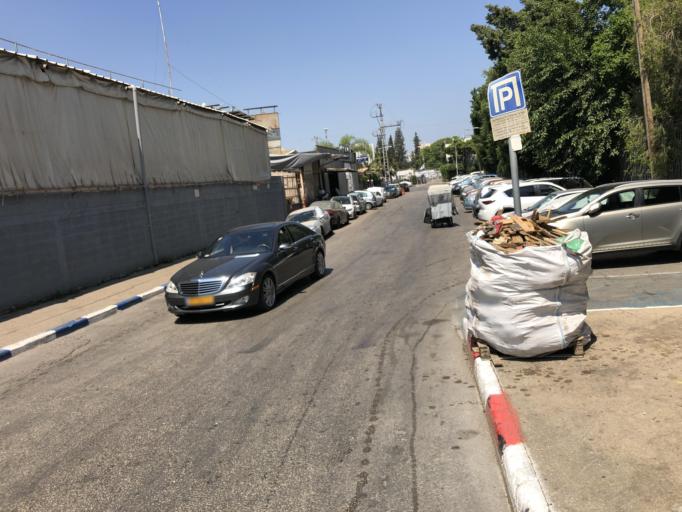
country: IL
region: Central District
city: Yehud
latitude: 32.0291
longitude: 34.9004
